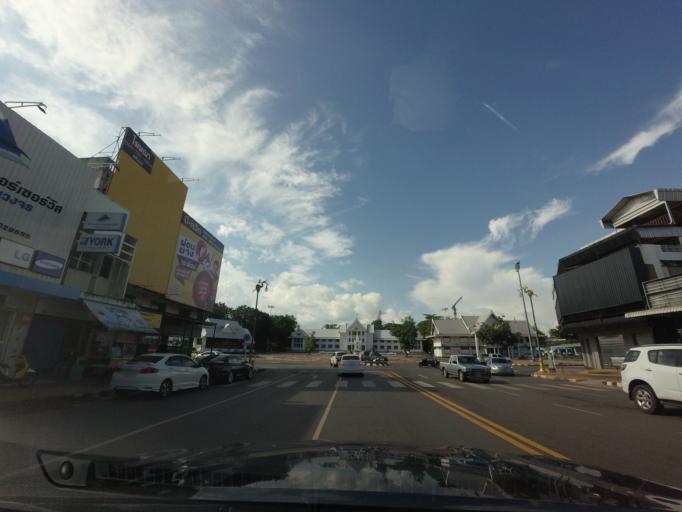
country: TH
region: Nong Khai
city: Nong Khai
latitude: 17.8785
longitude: 102.7411
